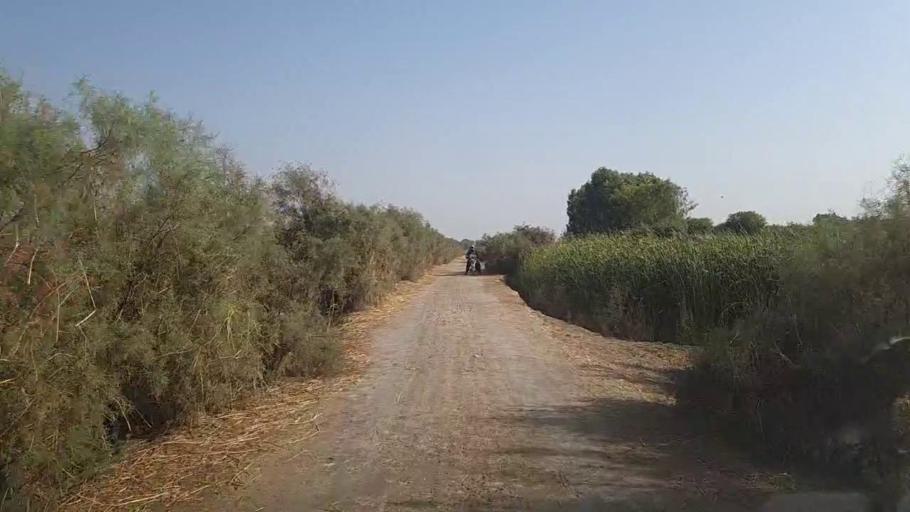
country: PK
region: Sindh
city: Kandhkot
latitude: 28.3563
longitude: 69.3342
